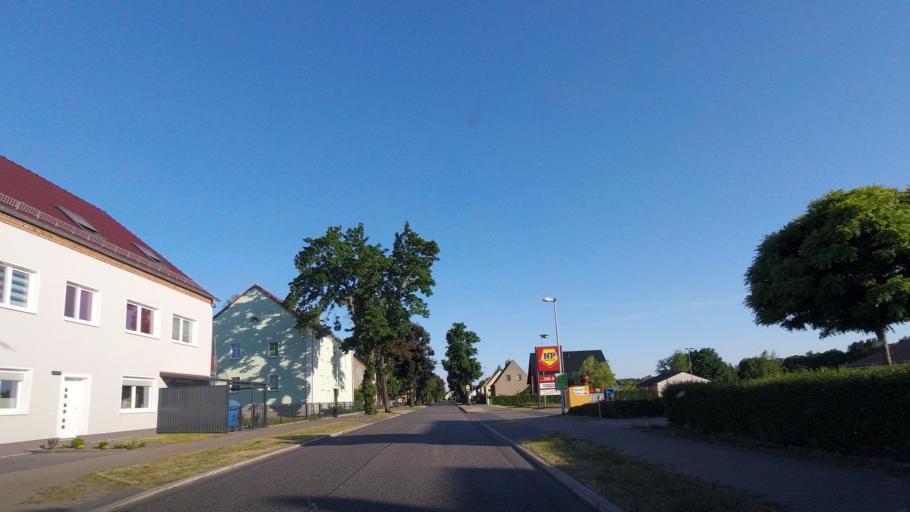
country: DE
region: Brandenburg
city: Golzow
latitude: 52.2836
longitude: 12.6026
